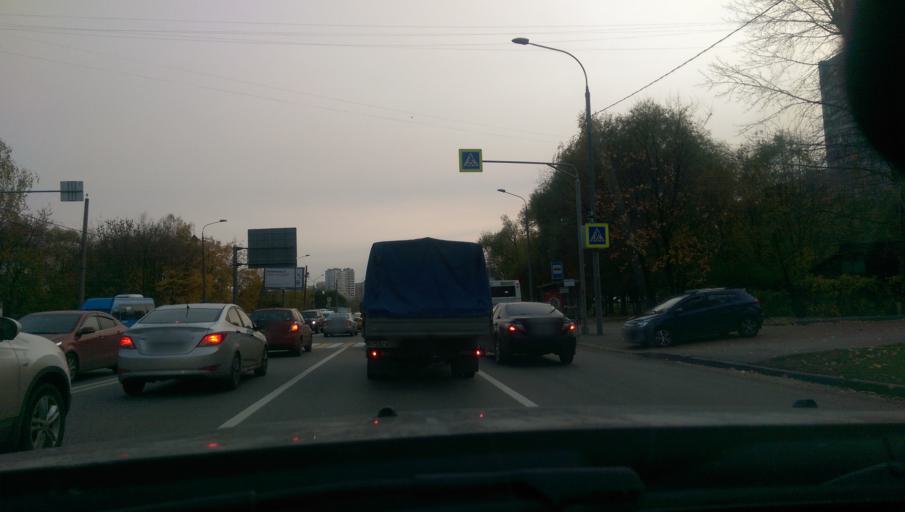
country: RU
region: Moscow
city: Vatutino
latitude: 55.8892
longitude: 37.6743
